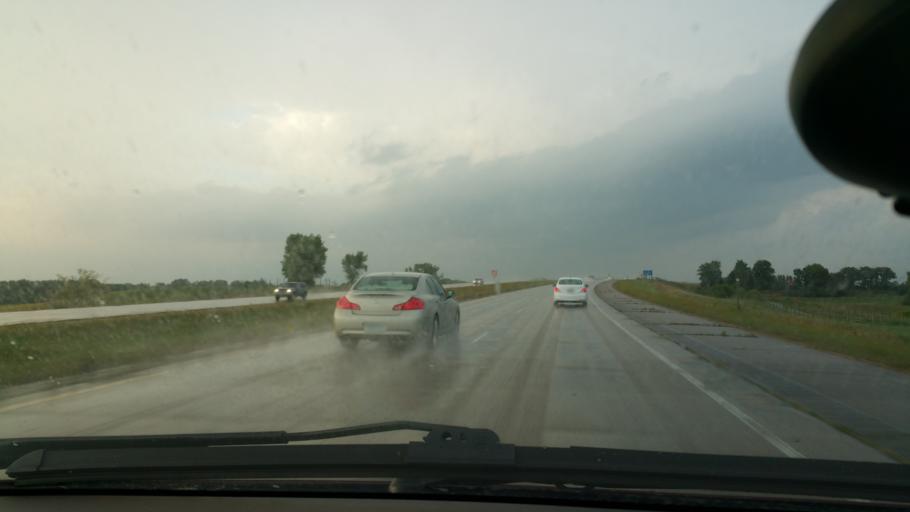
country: US
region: Minnesota
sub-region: Freeborn County
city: Albert Lea
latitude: 43.6449
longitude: -93.3232
